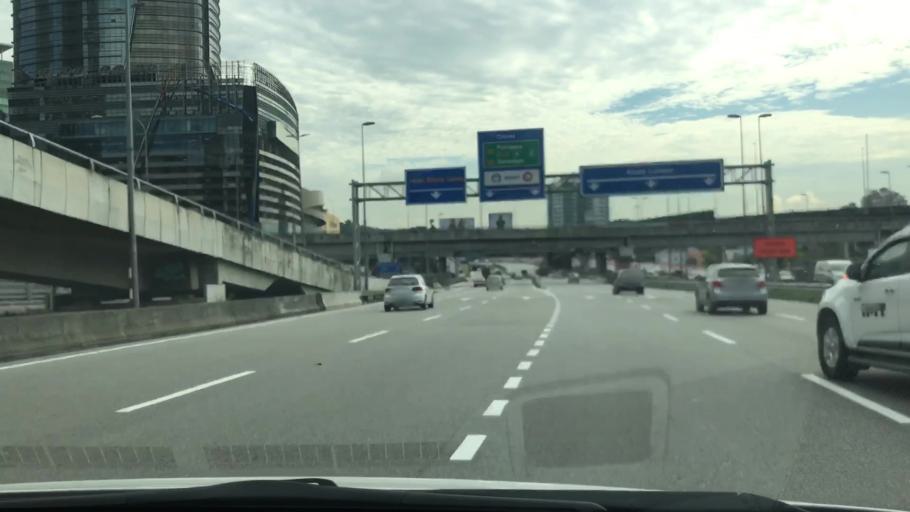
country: MY
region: Kuala Lumpur
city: Kuala Lumpur
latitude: 3.1149
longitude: 101.6735
